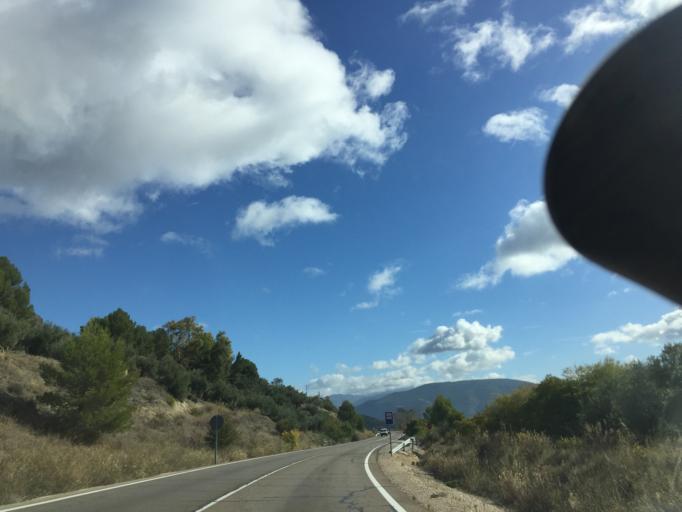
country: ES
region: Andalusia
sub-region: Provincia de Jaen
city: Jaen
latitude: 37.7493
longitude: -3.8100
